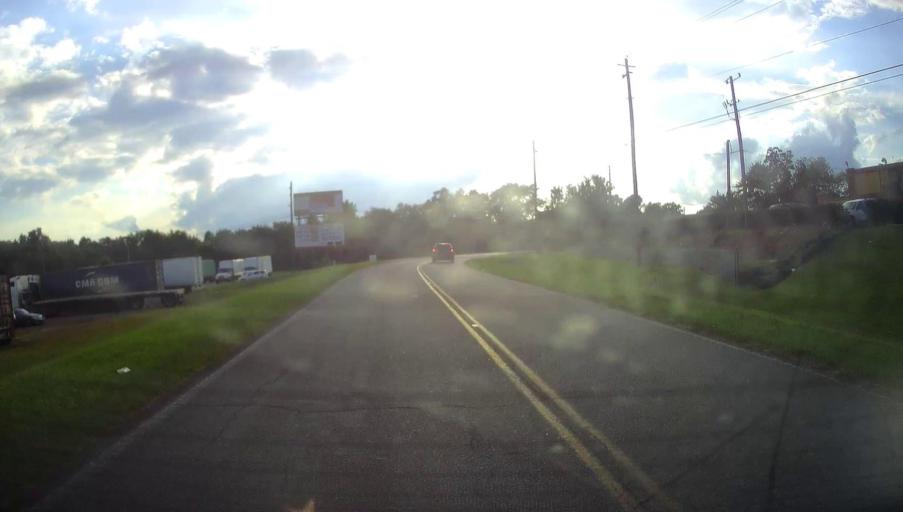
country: US
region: Georgia
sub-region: Monroe County
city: Forsyth
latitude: 33.0326
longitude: -83.9222
